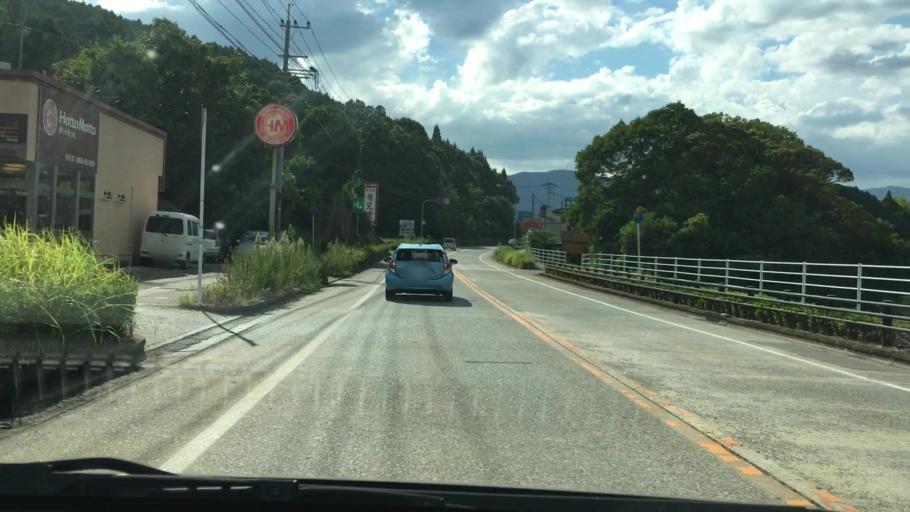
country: JP
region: Saga Prefecture
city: Imaricho-ko
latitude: 33.1821
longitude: 129.8774
